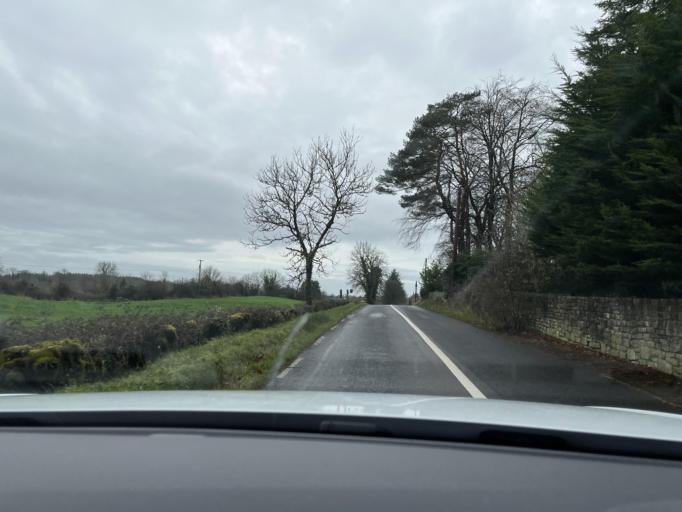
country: IE
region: Connaught
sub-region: County Leitrim
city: Manorhamilton
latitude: 54.2472
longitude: -8.2535
